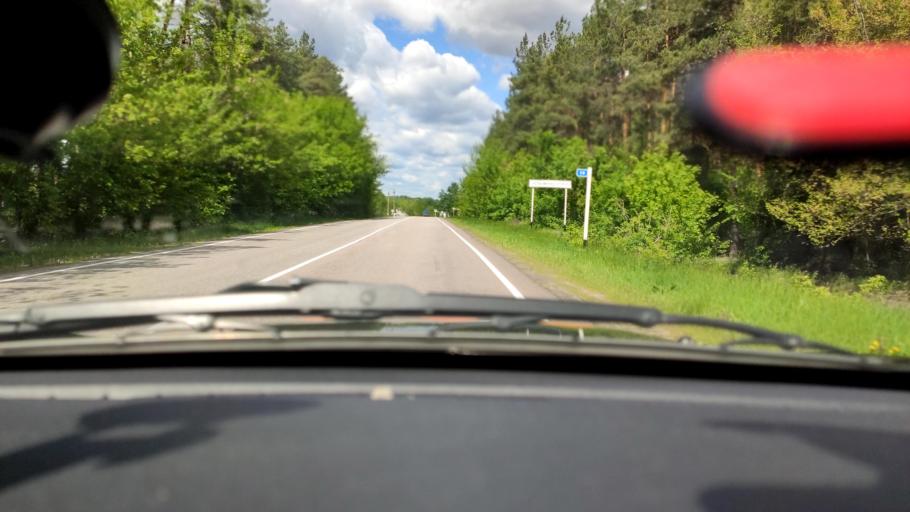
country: RU
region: Belgorod
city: Krasnoye
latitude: 51.0577
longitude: 38.8445
